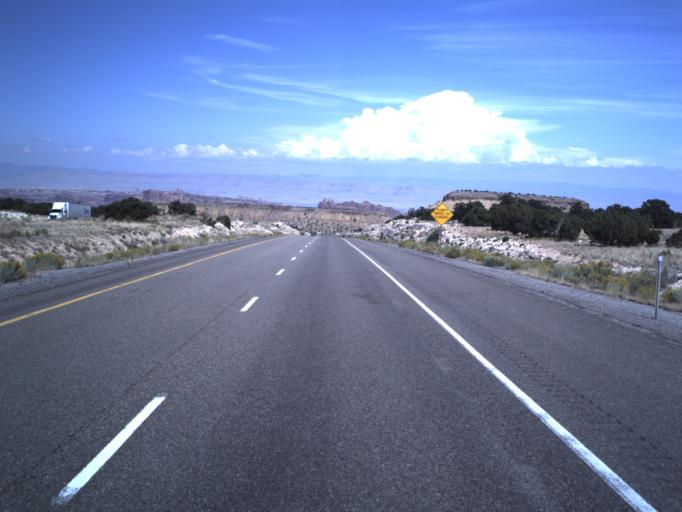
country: US
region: Utah
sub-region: Emery County
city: Castle Dale
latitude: 38.9065
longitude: -110.5313
